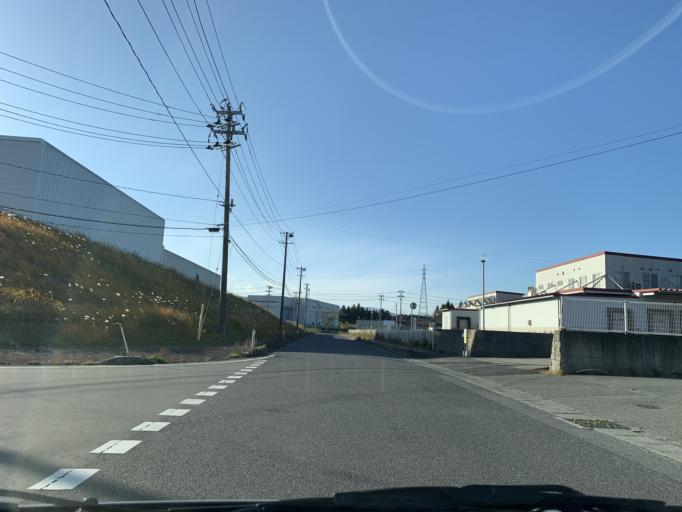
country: JP
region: Iwate
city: Kitakami
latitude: 39.2473
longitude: 141.0939
